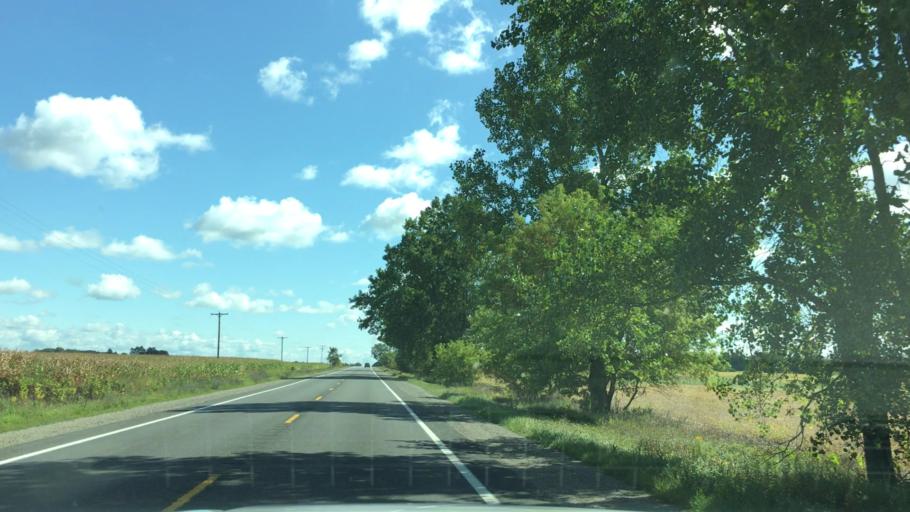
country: US
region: Michigan
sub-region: Montcalm County
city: Carson City
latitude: 43.1773
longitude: -84.9062
